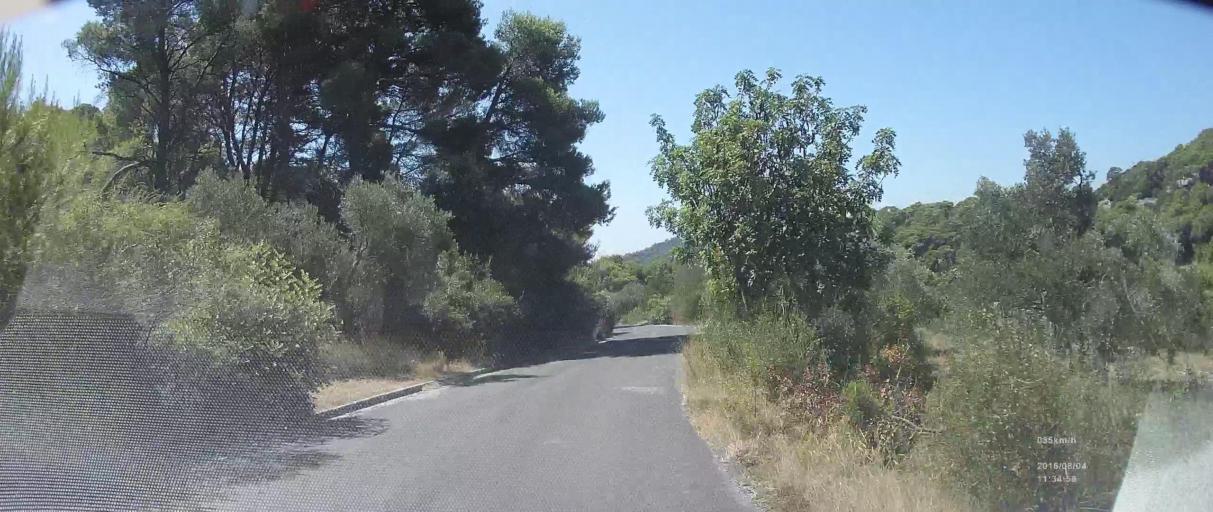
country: HR
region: Dubrovacko-Neretvanska
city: Blato
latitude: 42.7824
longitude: 17.3673
